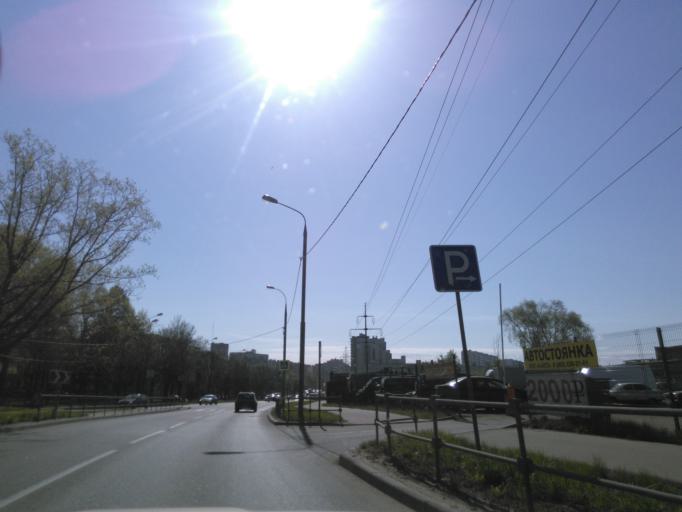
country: RU
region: Moscow
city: Zelenograd
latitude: 56.0093
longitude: 37.1941
